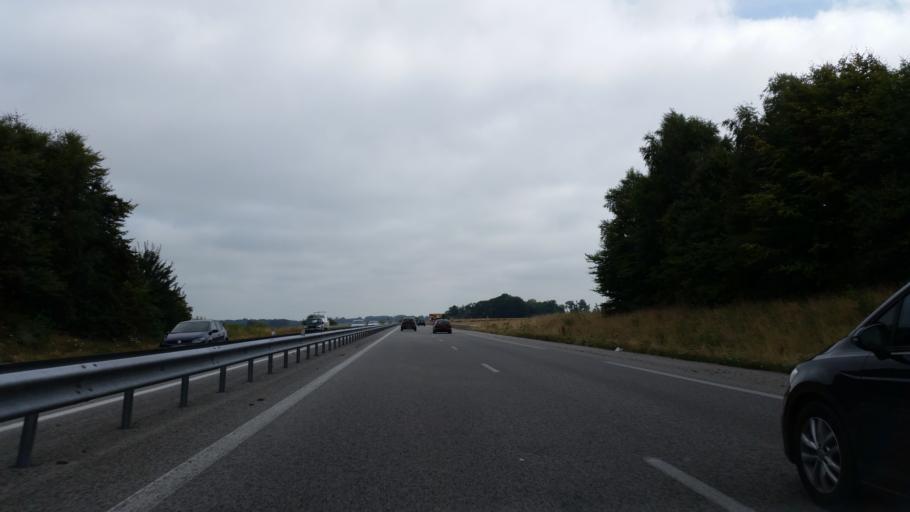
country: FR
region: Haute-Normandie
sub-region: Departement de la Seine-Maritime
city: Sainte-Marie-des-Champs
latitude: 49.6507
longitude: 0.7908
